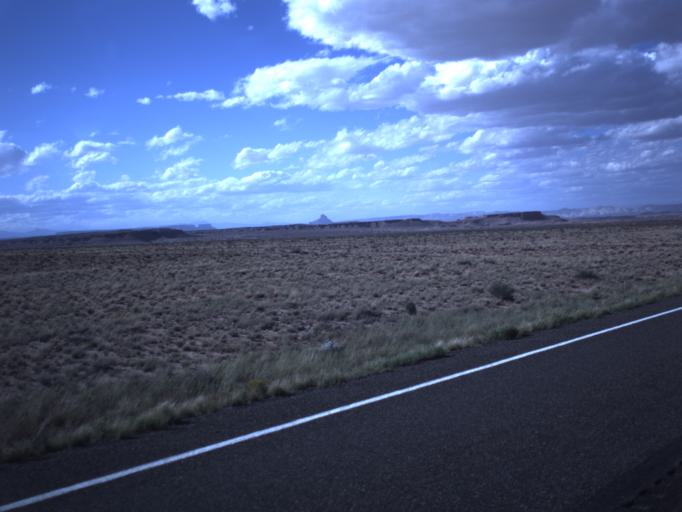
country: US
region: Utah
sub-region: Emery County
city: Ferron
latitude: 38.2867
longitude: -110.6644
